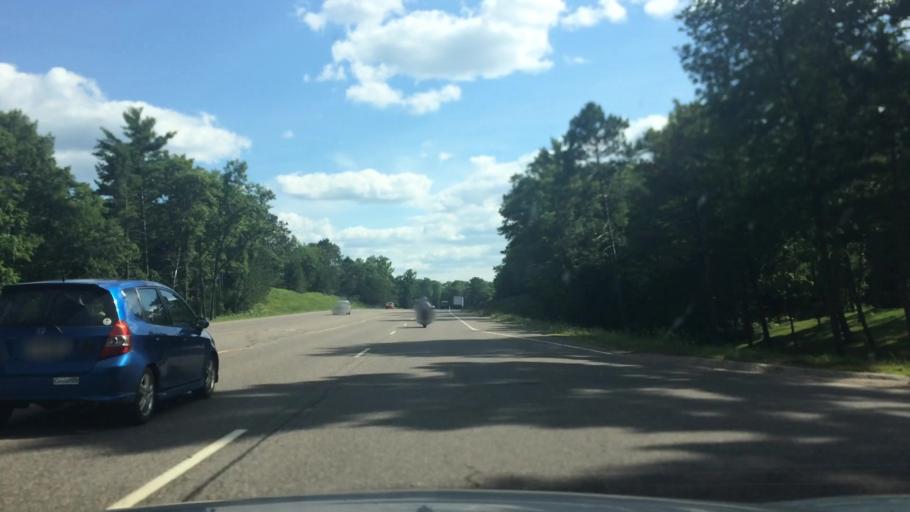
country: US
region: Wisconsin
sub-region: Vilas County
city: Lac du Flambeau
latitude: 45.8422
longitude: -89.7069
